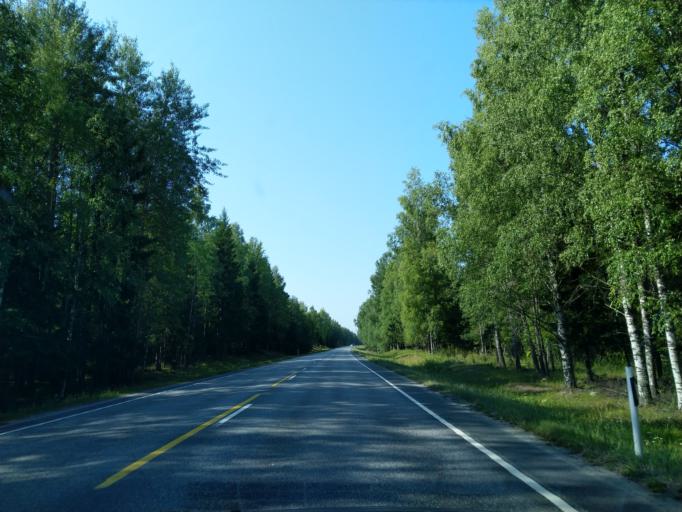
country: FI
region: Satakunta
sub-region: Pori
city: Pomarkku
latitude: 61.6404
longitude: 21.9456
